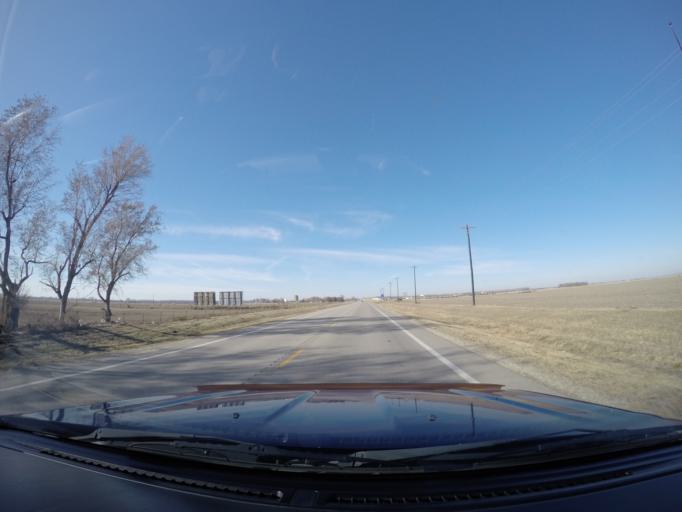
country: US
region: Kansas
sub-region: Clay County
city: Clay Center
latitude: 39.3798
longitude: -97.1518
